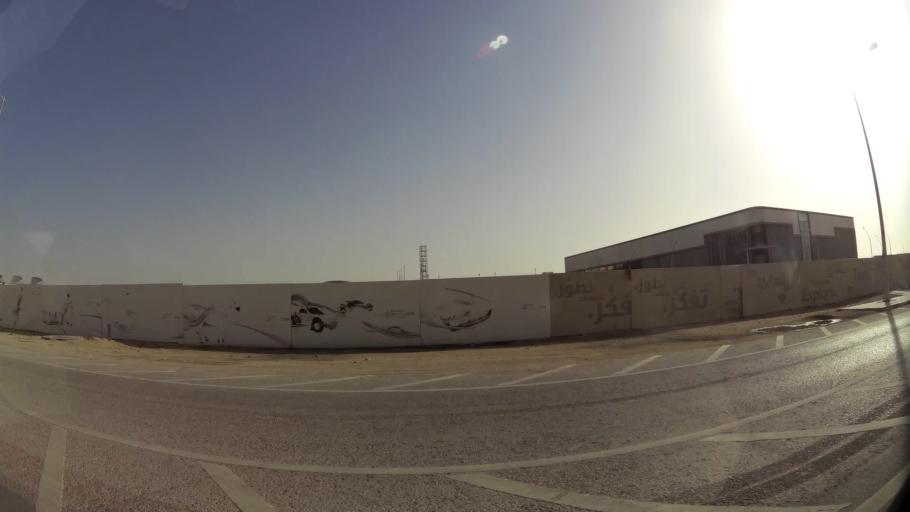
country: QA
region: Baladiyat ar Rayyan
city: Ar Rayyan
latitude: 25.3310
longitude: 51.4382
